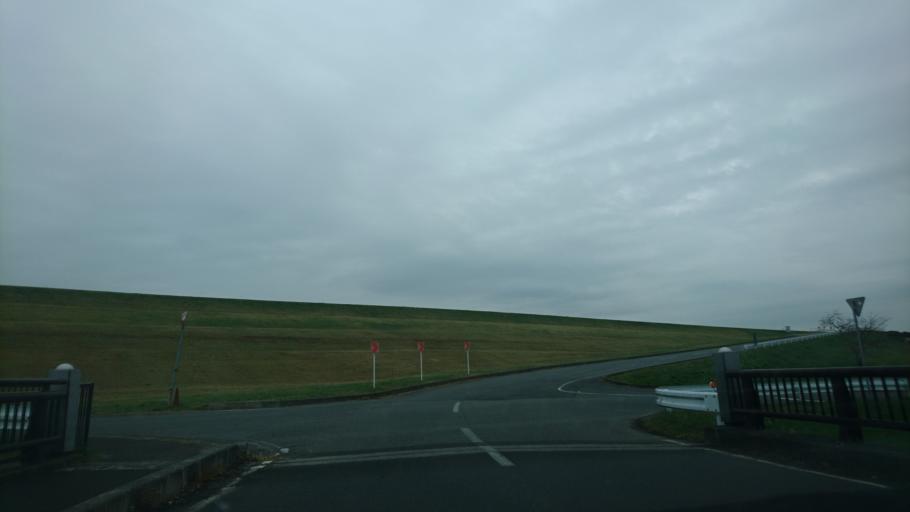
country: JP
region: Iwate
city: Ichinoseki
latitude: 38.9420
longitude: 141.1558
